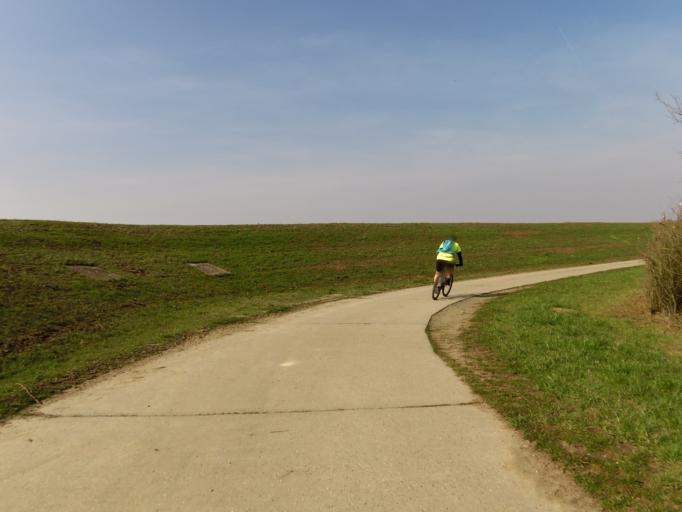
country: DE
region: Hesse
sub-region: Regierungsbezirk Darmstadt
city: Biblis
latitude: 49.7179
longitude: 8.4516
